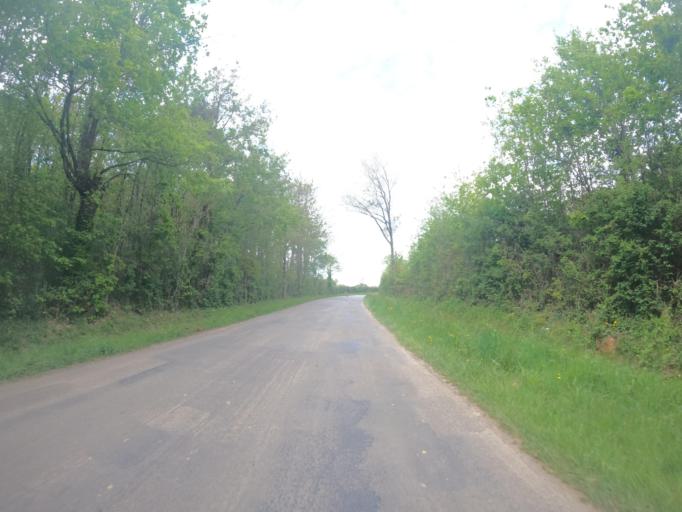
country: FR
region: Poitou-Charentes
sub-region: Departement des Deux-Sevres
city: Saint-Varent
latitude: 46.8850
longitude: -0.2937
